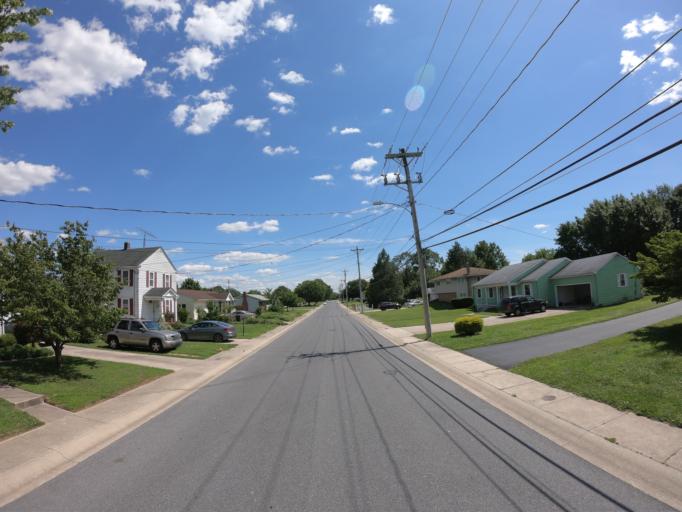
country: US
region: Delaware
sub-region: Sussex County
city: Milford
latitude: 38.9243
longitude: -75.4275
